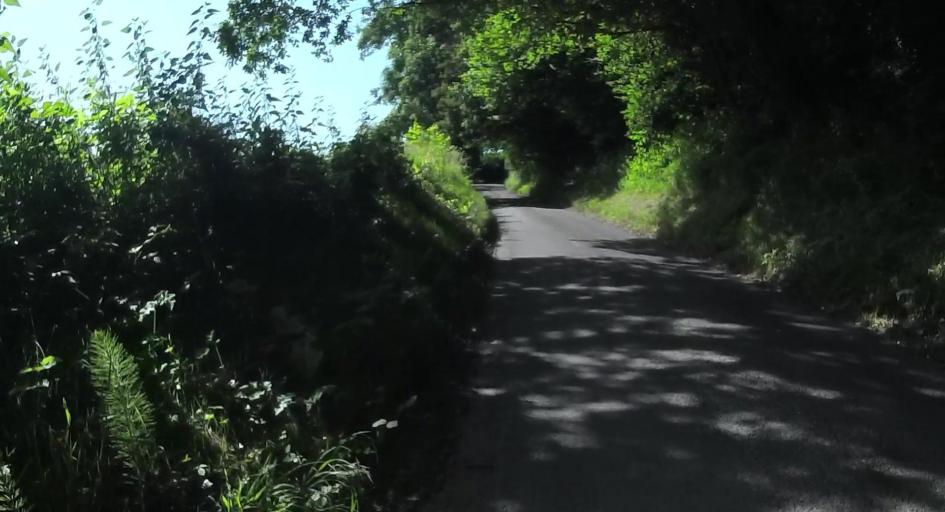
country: GB
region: England
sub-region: Hampshire
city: Kingsley
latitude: 51.1578
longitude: -0.8951
